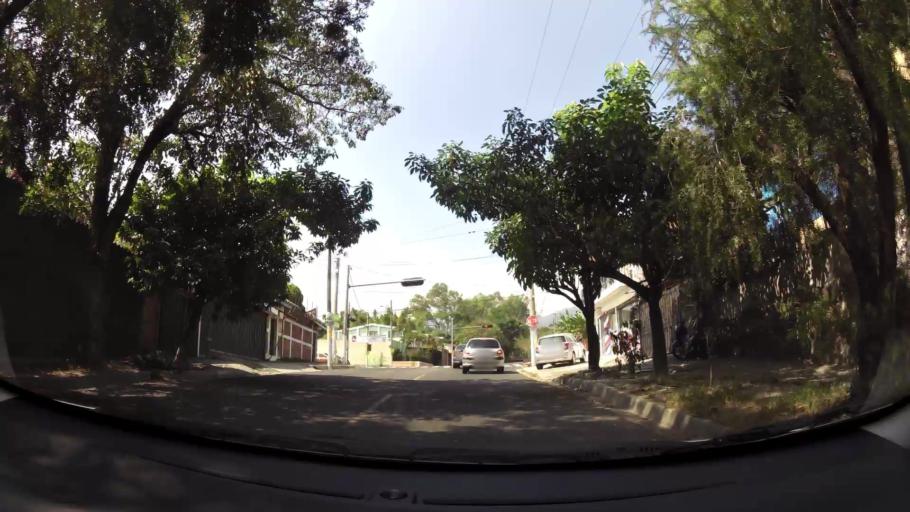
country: SV
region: San Salvador
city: Mejicanos
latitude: 13.7097
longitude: -89.2195
